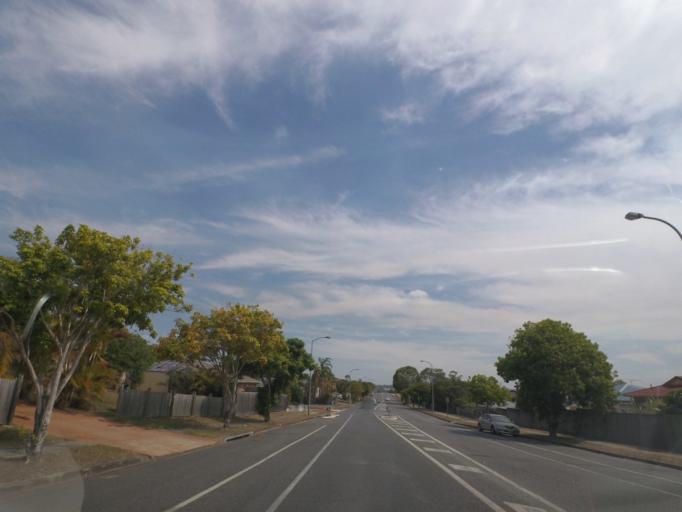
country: AU
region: Queensland
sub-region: Brisbane
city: Sunnybank Hills
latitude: -27.6206
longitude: 153.0604
